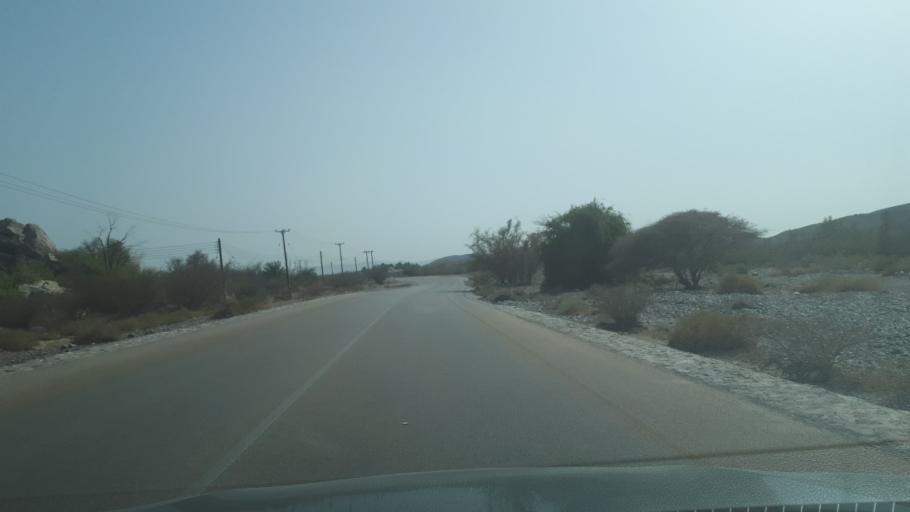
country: OM
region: Az Zahirah
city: `Ibri
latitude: 23.1459
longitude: 56.8979
